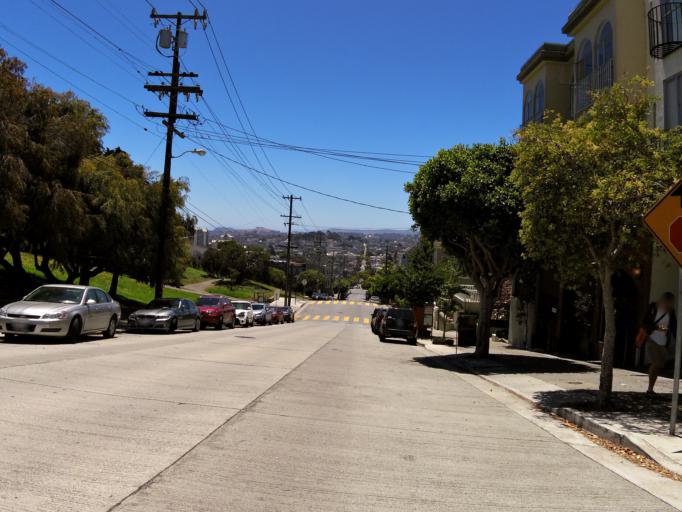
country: US
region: California
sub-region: San Francisco County
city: San Francisco
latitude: 37.7916
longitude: -122.4395
